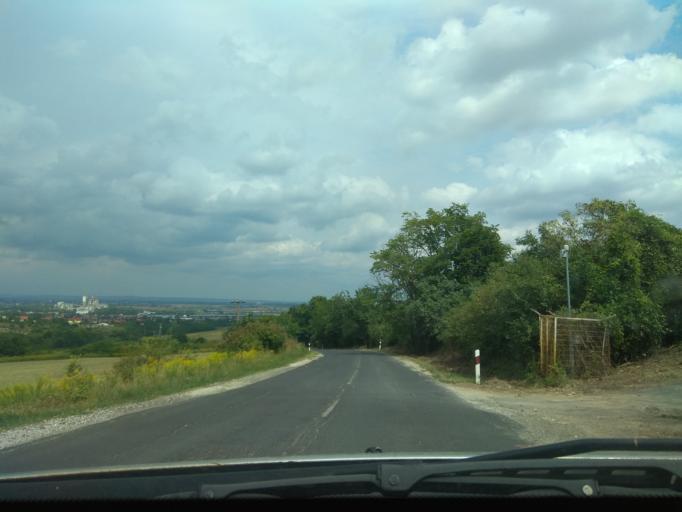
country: HU
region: Borsod-Abauj-Zemplen
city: Malyi
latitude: 48.0398
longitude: 20.7858
